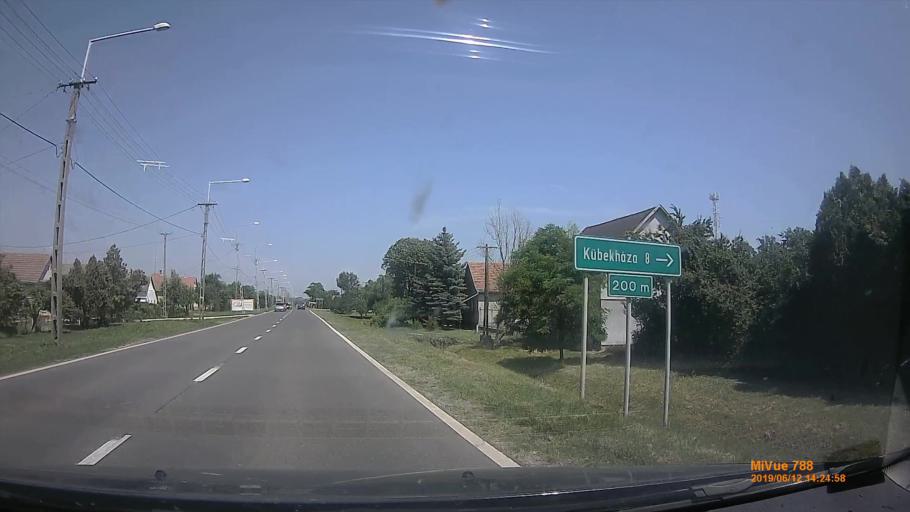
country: HU
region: Csongrad
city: Maroslele
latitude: 46.2186
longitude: 20.3207
